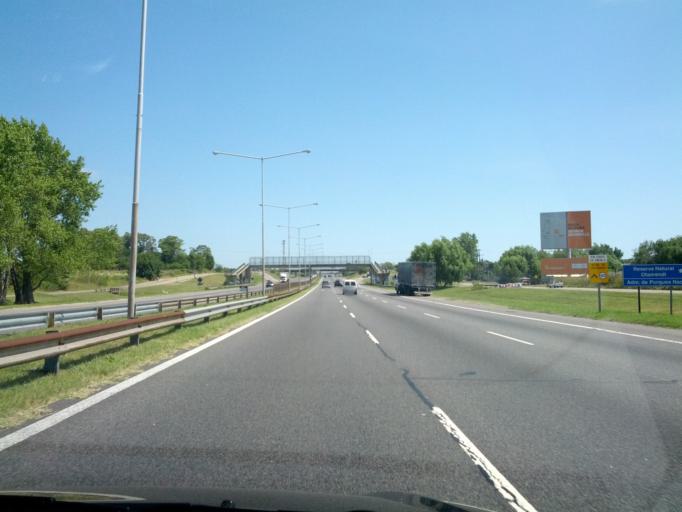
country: AR
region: Buenos Aires
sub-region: Partido de Campana
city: Campana
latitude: -34.2320
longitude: -58.9143
